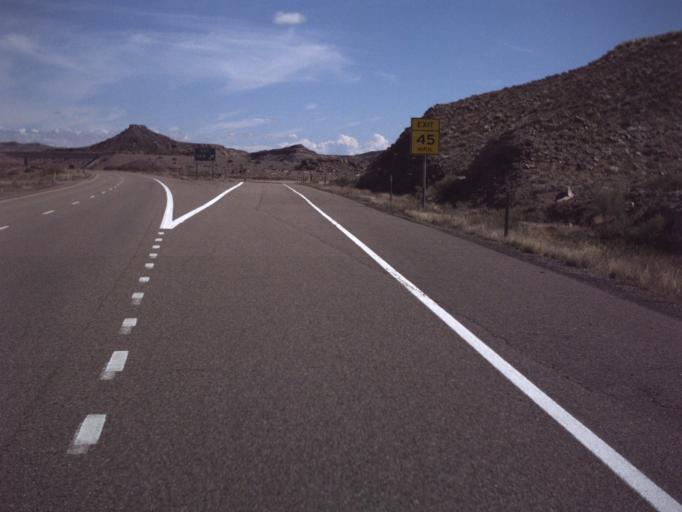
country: US
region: Utah
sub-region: Carbon County
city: East Carbon City
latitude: 38.9214
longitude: -110.3837
